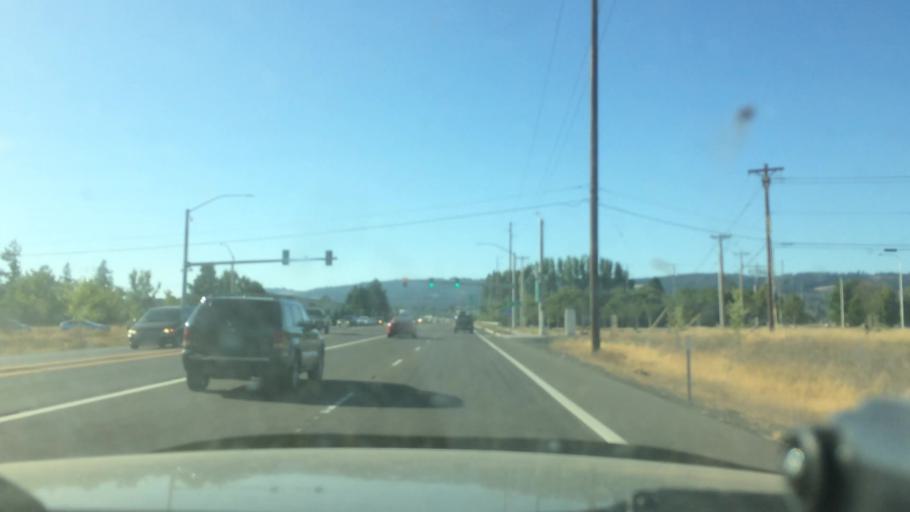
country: US
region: Oregon
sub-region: Yamhill County
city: Newberg
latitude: 45.2895
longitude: -122.9471
